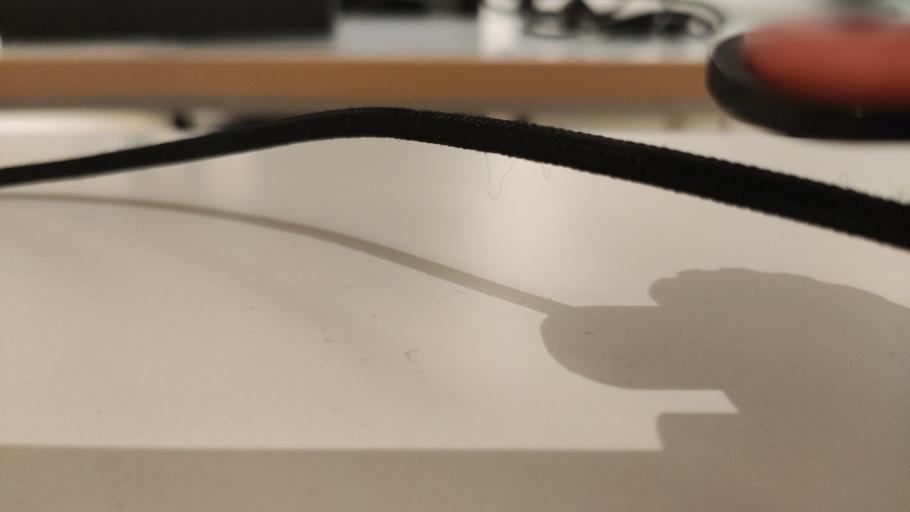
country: RU
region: Moskovskaya
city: Dorokhovo
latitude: 55.4232
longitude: 36.3593
